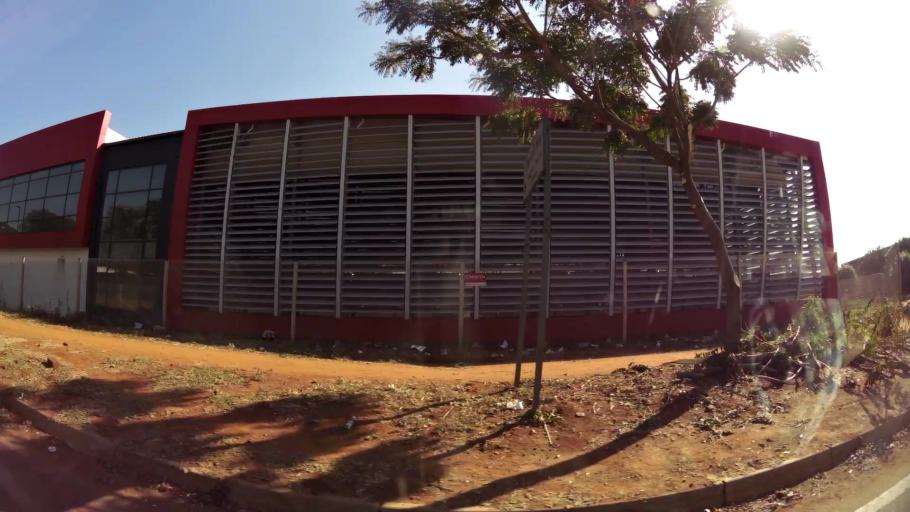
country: ZA
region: Gauteng
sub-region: City of Tshwane Metropolitan Municipality
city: Pretoria
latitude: -25.6806
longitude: 28.1917
